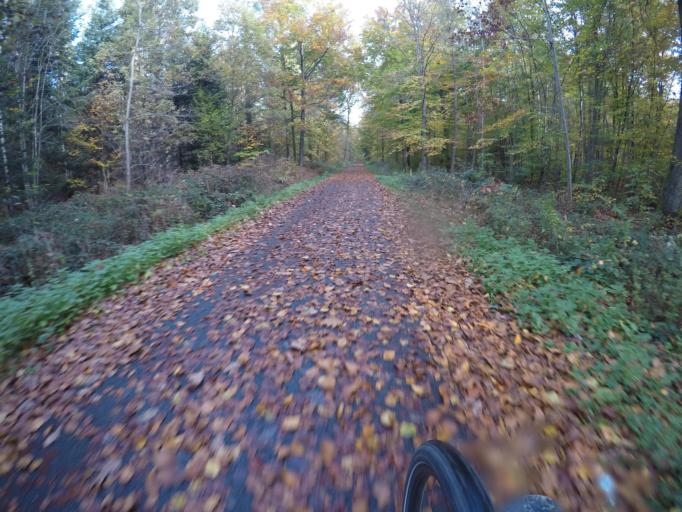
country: DE
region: Baden-Wuerttemberg
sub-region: Regierungsbezirk Stuttgart
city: Sindelfingen
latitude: 48.7330
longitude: 9.0091
